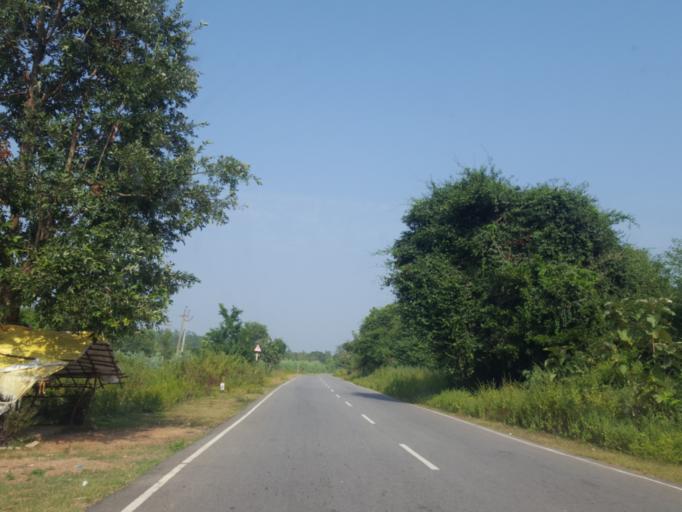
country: IN
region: Telangana
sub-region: Khammam
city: Yellandu
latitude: 17.6253
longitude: 80.3053
